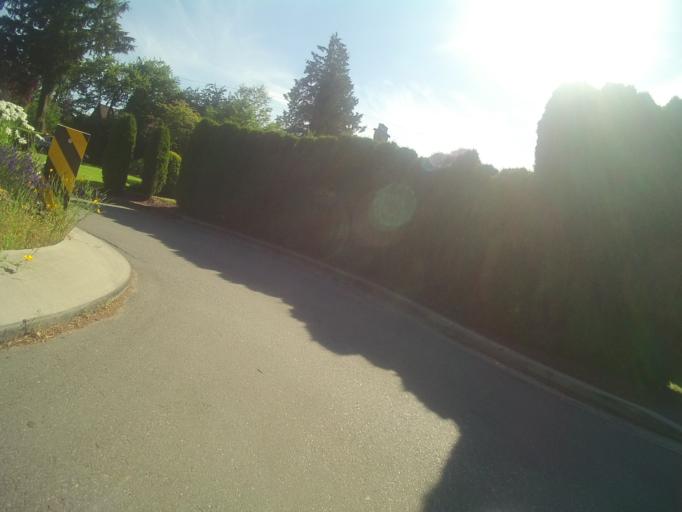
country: CA
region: British Columbia
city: Vancouver
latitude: 49.2178
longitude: -123.1483
